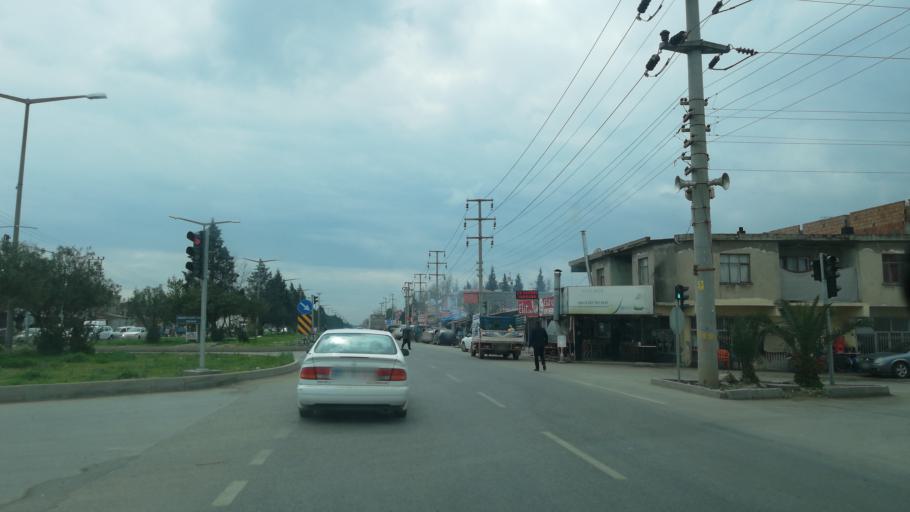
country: TR
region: Kahramanmaras
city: Turkoglu
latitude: 37.4127
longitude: 36.8793
